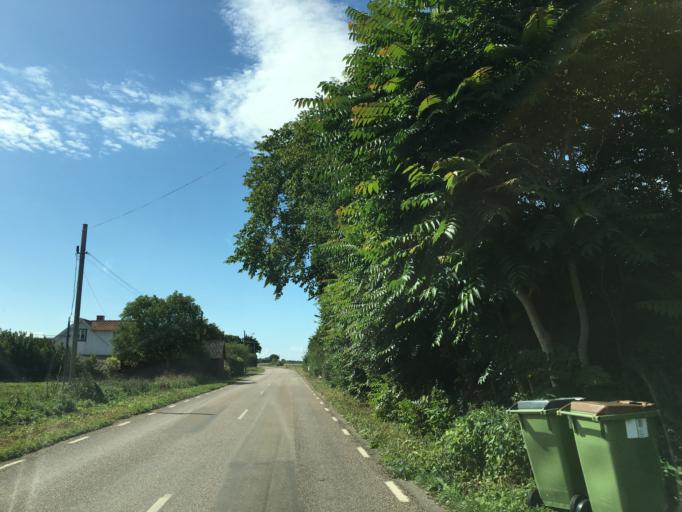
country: SE
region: Kalmar
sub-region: Morbylanga Kommun
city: Moerbylanga
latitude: 56.3880
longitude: 16.4122
